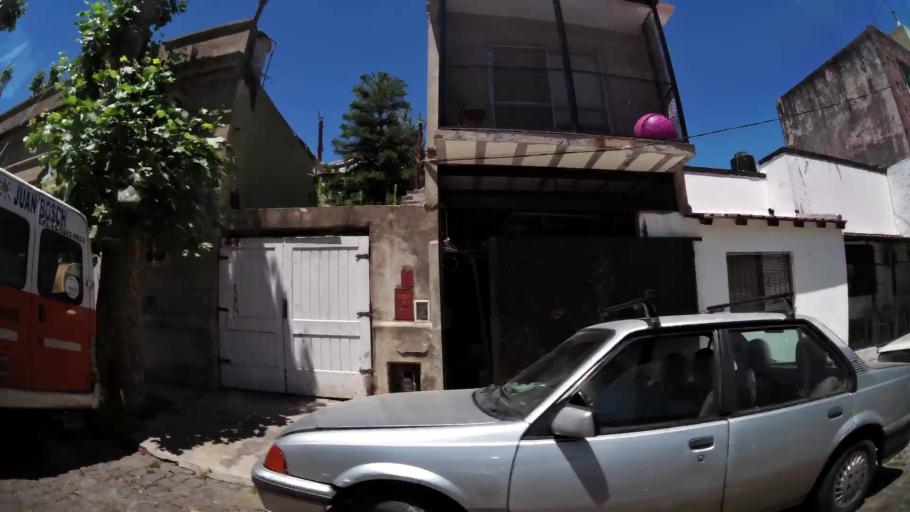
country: AR
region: Buenos Aires
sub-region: Partido de Tigre
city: Tigre
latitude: -34.4469
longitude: -58.5542
